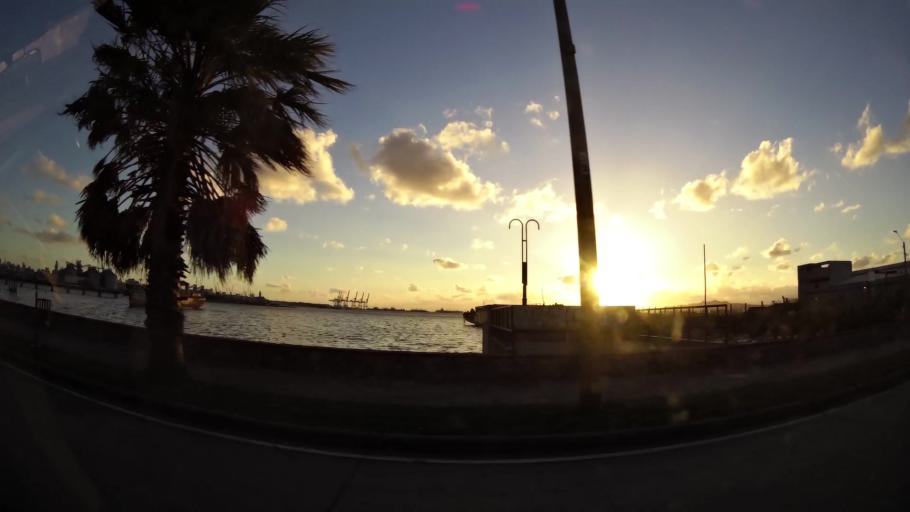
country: UY
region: Montevideo
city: Montevideo
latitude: -34.8829
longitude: -56.1998
